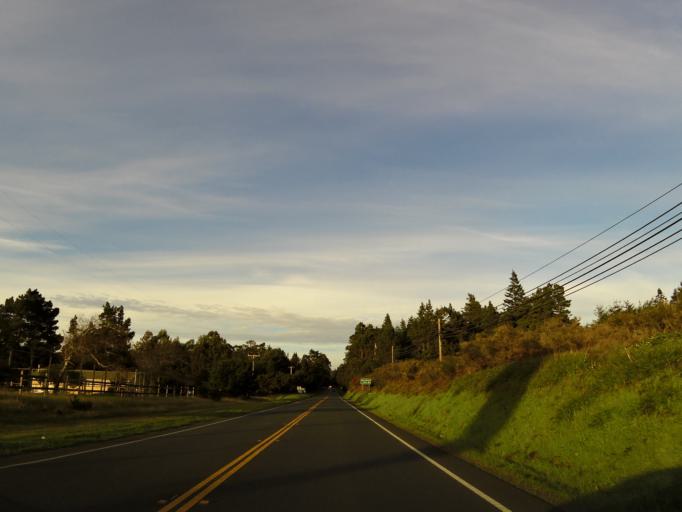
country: US
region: California
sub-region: Mendocino County
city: Fort Bragg
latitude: 39.3888
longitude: -123.8121
